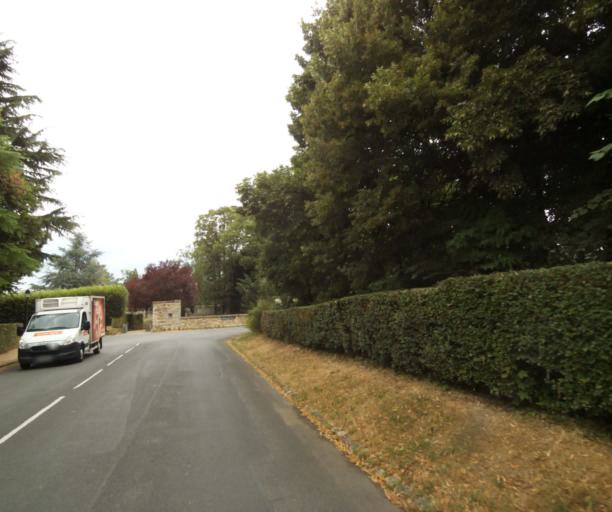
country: FR
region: Ile-de-France
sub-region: Departement de Seine-et-Marne
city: Cely
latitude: 48.4469
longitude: 2.5503
